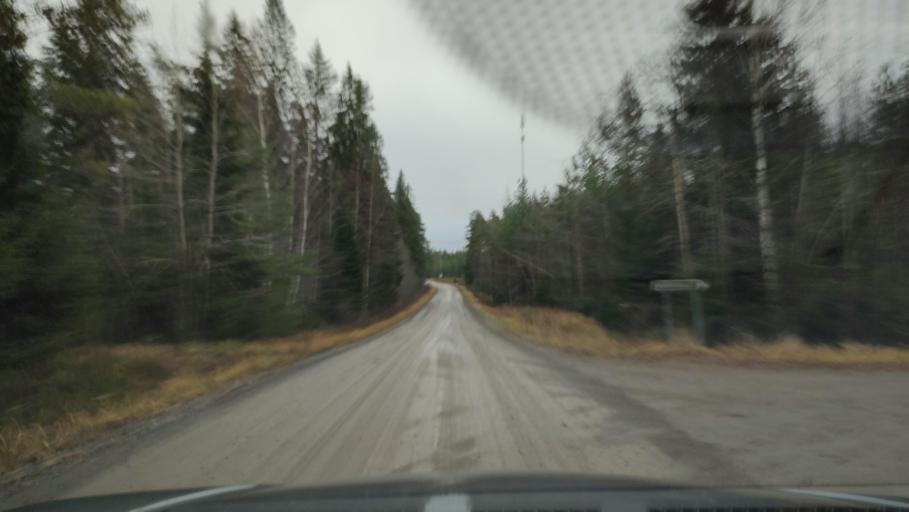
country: FI
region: Southern Ostrobothnia
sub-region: Suupohja
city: Karijoki
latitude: 62.1374
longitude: 21.6608
